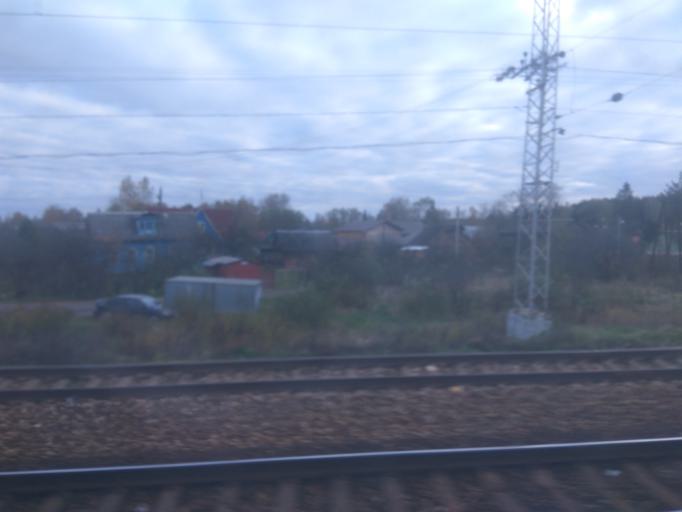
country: RU
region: Moskovskaya
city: Aprelevka
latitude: 55.5767
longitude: 37.1067
